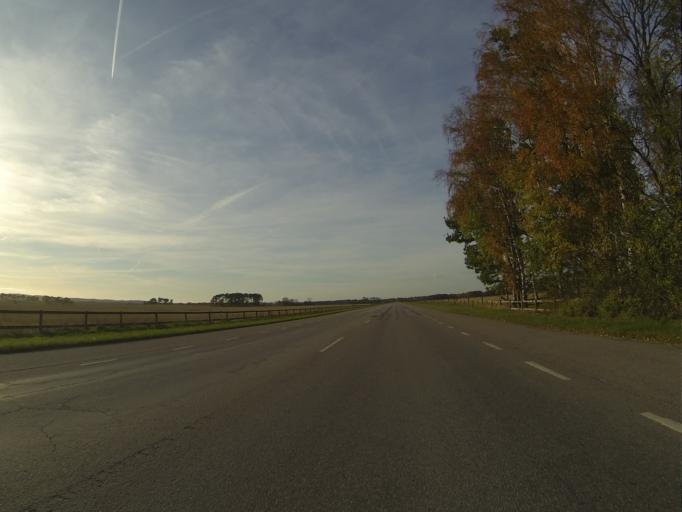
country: SE
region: Skane
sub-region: Hoors Kommun
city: Loberod
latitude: 55.7260
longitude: 13.4446
